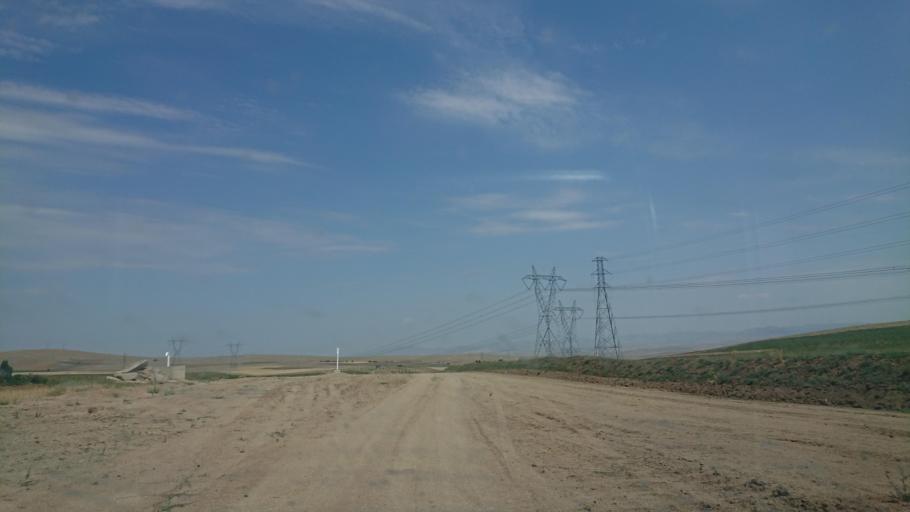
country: TR
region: Aksaray
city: Agacoren
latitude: 38.8996
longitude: 33.9250
